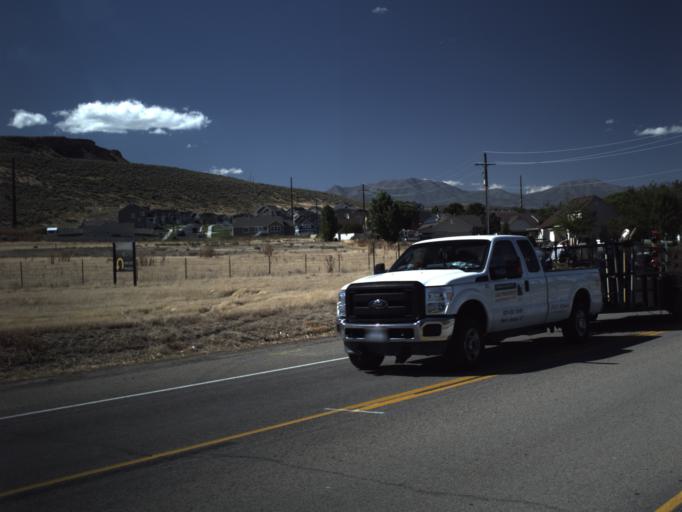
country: US
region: Utah
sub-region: Utah County
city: Saratoga Springs
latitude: 40.3326
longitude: -111.9116
